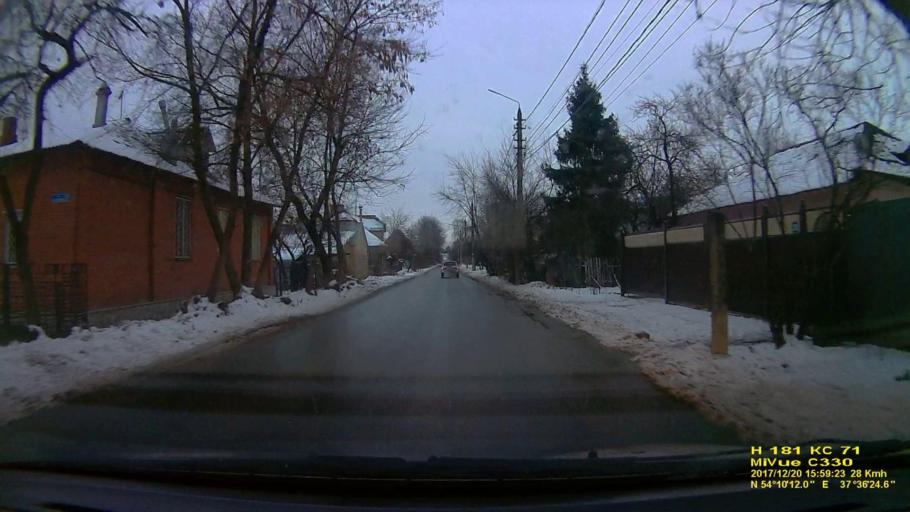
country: RU
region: Tula
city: Tula
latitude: 54.1699
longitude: 37.6071
